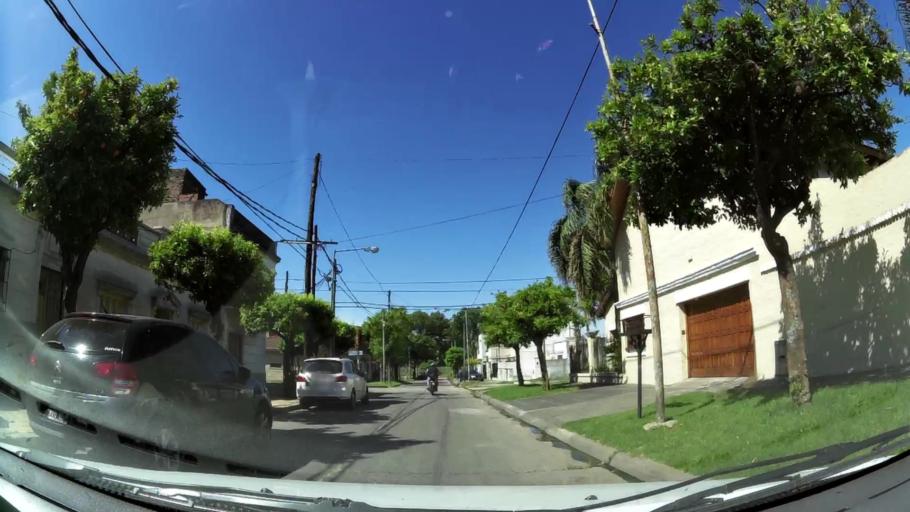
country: AR
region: Buenos Aires
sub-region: Partido de General San Martin
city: General San Martin
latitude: -34.5381
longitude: -58.5740
